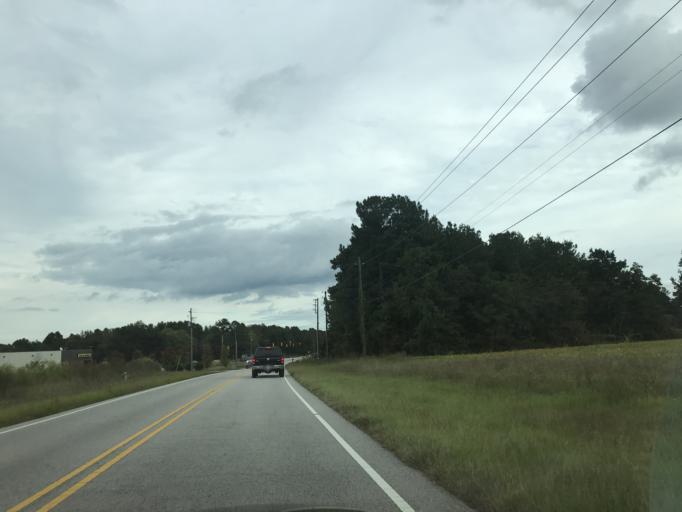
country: US
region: North Carolina
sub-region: Wake County
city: Rolesville
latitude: 35.9830
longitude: -78.3848
